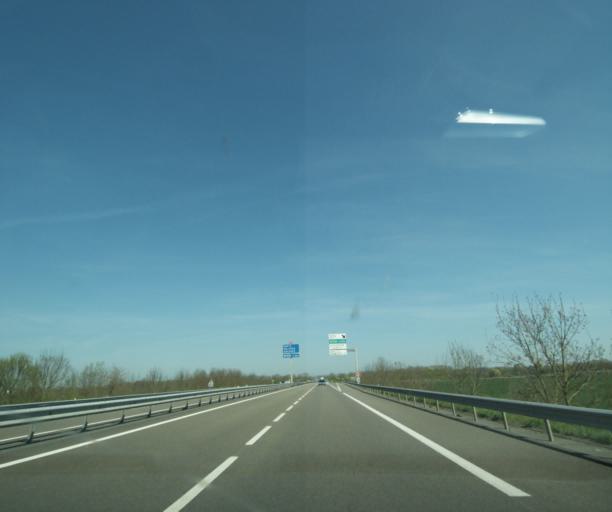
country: FR
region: Bourgogne
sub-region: Departement de la Nievre
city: Sermoise-sur-Loire
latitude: 46.9531
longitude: 3.1698
